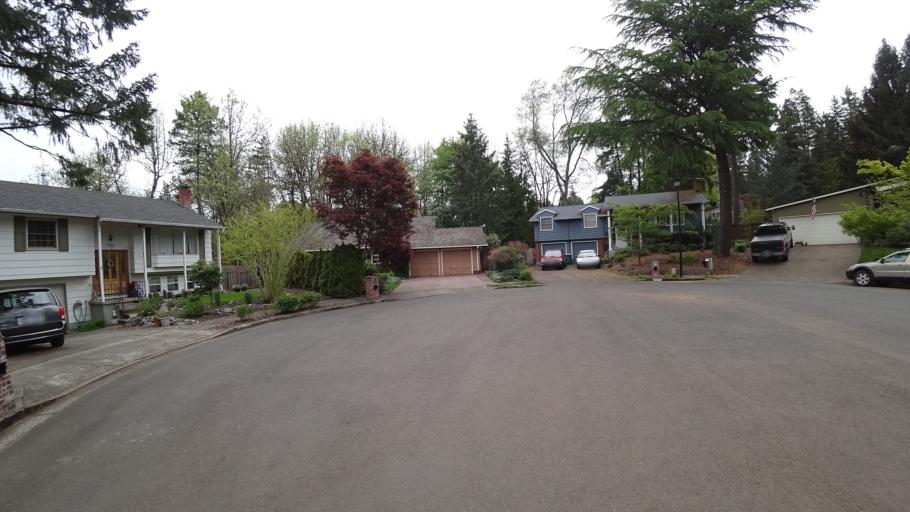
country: US
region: Oregon
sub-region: Washington County
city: Beaverton
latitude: 45.4645
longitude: -122.8195
